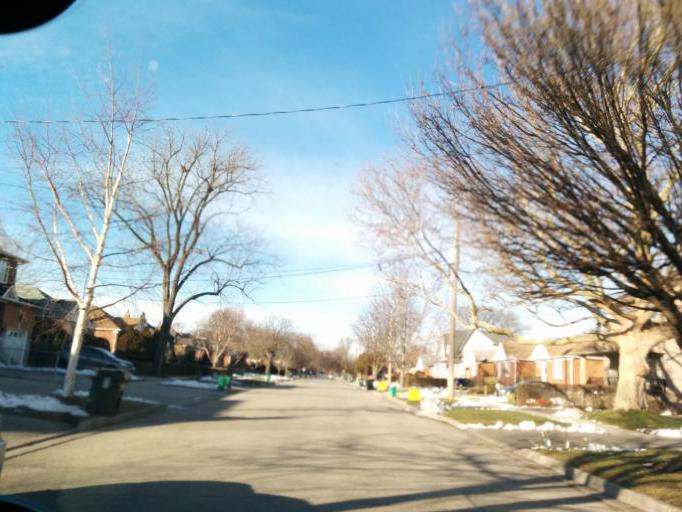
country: CA
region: Ontario
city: Etobicoke
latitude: 43.6061
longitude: -79.5384
